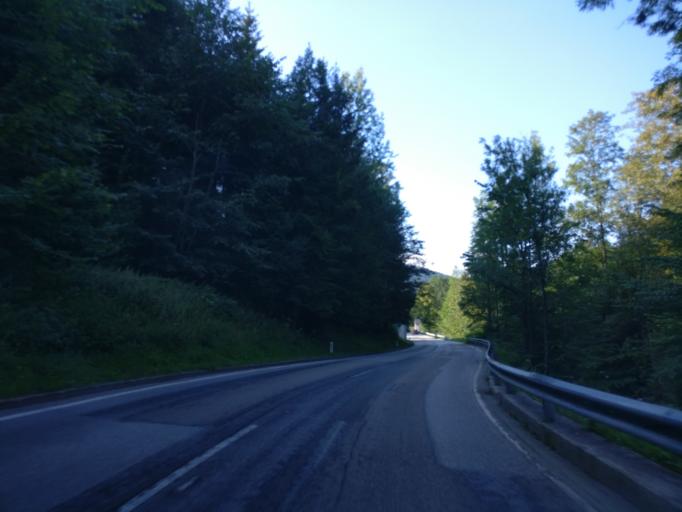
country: AT
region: Lower Austria
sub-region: Politischer Bezirk Scheibbs
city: Gostling an der Ybbs
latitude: 47.7702
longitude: 14.9063
